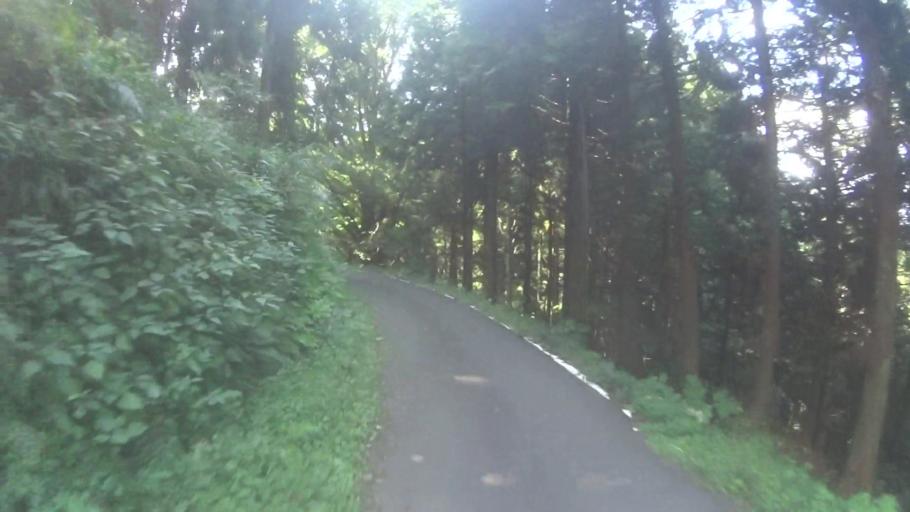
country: JP
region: Kyoto
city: Miyazu
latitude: 35.7140
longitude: 135.1666
